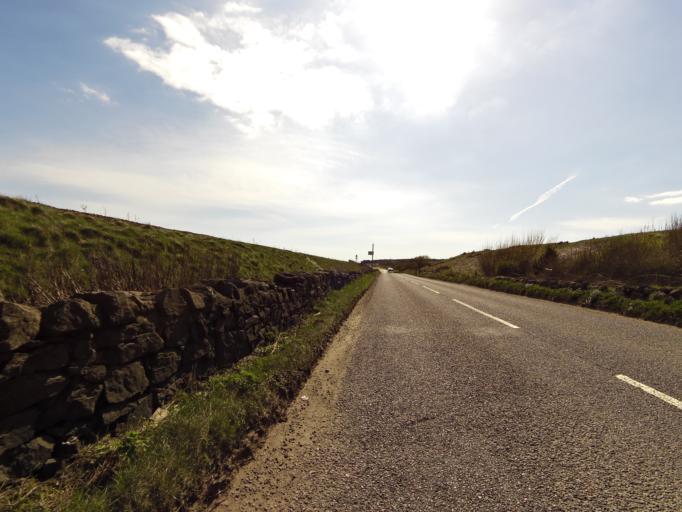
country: GB
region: Scotland
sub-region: Aberdeen City
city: Aberdeen
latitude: 57.1183
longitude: -2.0612
